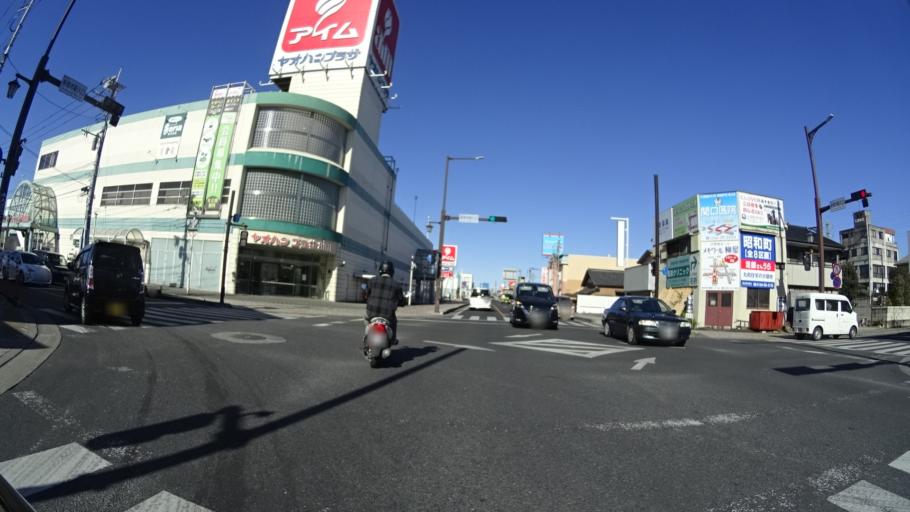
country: JP
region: Tochigi
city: Tochigi
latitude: 36.3900
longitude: 139.7361
